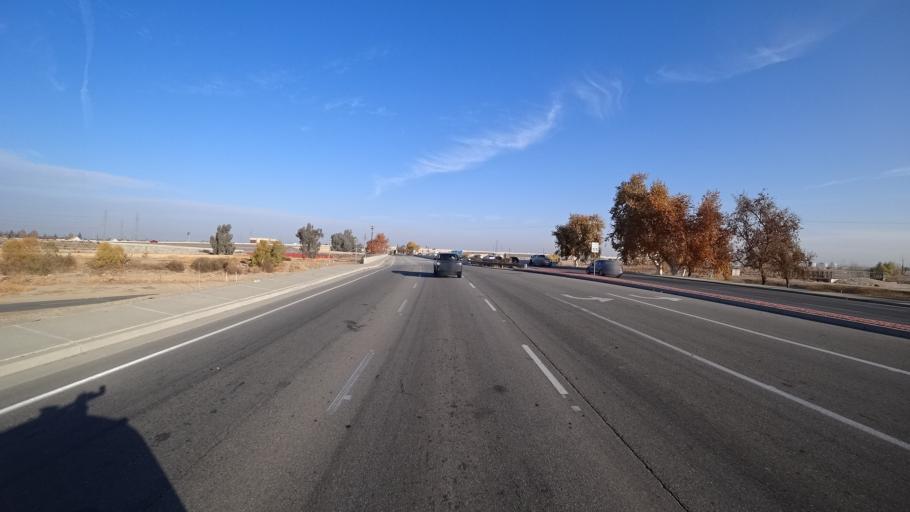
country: US
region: California
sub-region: Kern County
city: Greenacres
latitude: 35.3625
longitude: -119.0919
